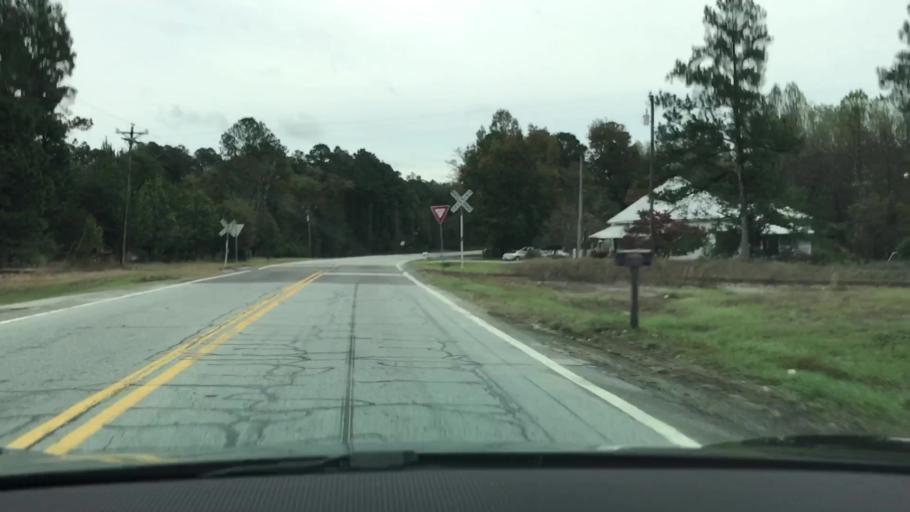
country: US
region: Georgia
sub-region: Warren County
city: Warrenton
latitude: 33.3868
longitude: -82.6335
